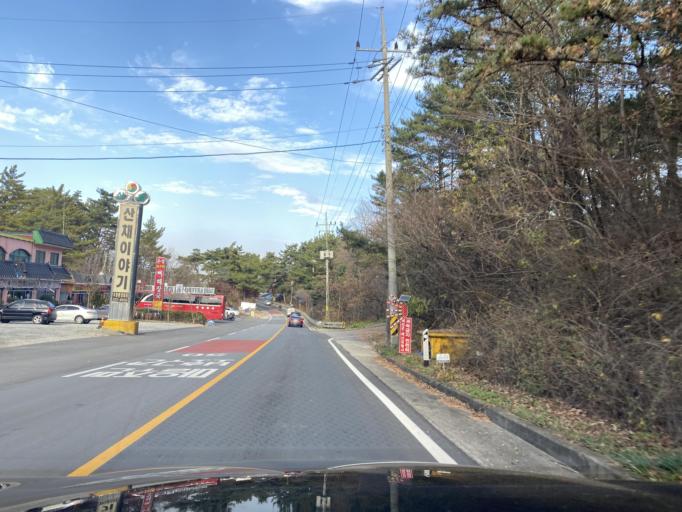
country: KR
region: Chungcheongnam-do
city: Hongsung
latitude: 36.6710
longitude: 126.6414
